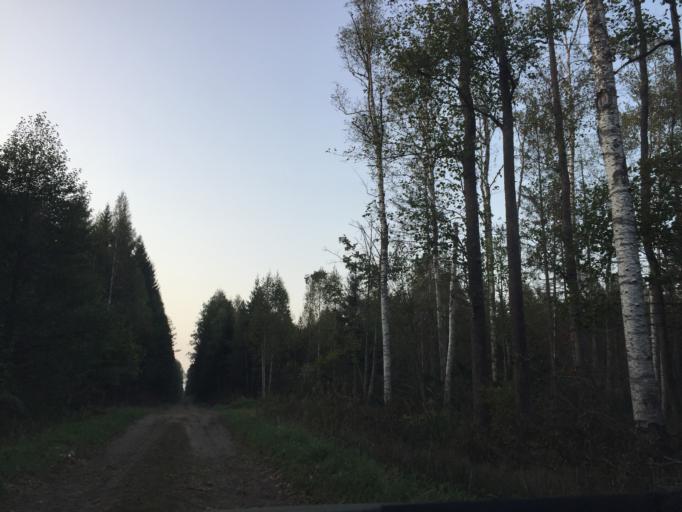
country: LV
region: Ikskile
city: Ikskile
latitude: 56.9336
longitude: 24.4832
